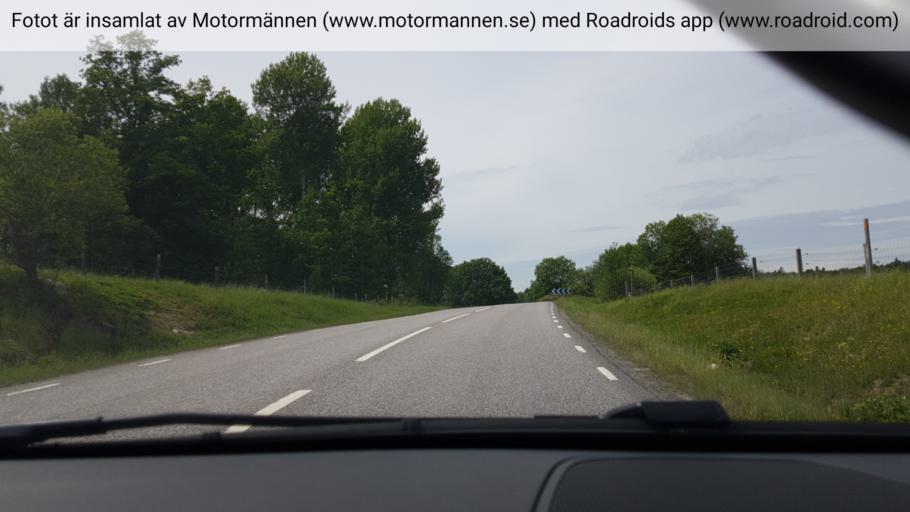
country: SE
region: Stockholm
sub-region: Haninge Kommun
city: Jordbro
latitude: 59.1784
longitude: 18.0844
